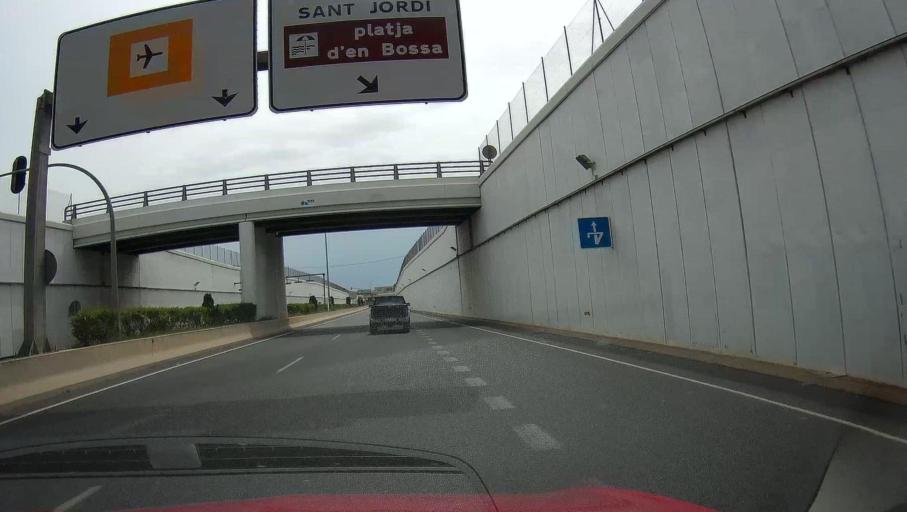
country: ES
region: Balearic Islands
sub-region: Illes Balears
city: Ibiza
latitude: 38.9009
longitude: 1.4051
